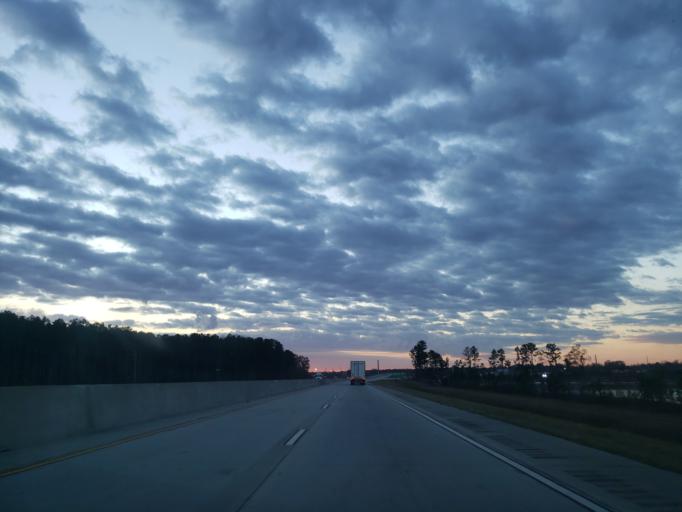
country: US
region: Georgia
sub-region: Chatham County
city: Port Wentworth
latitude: 32.1426
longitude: -81.1699
